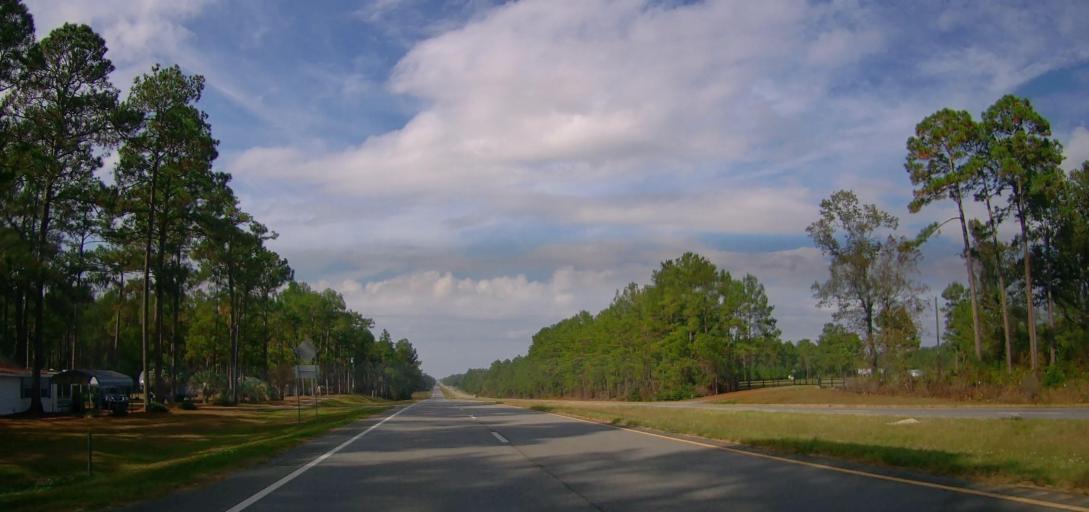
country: US
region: Georgia
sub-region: Thomas County
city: Thomasville
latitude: 30.9516
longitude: -84.0252
